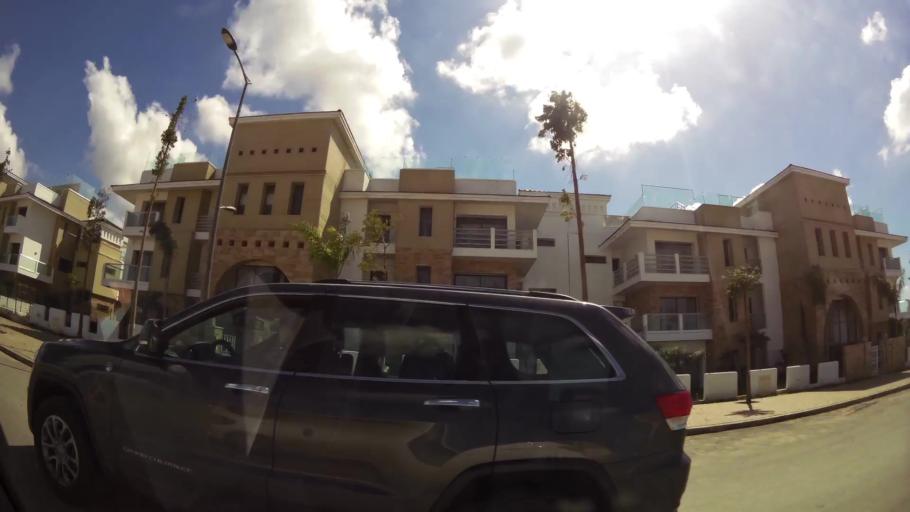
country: MA
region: Grand Casablanca
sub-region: Nouaceur
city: Bouskoura
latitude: 33.4859
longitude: -7.5990
